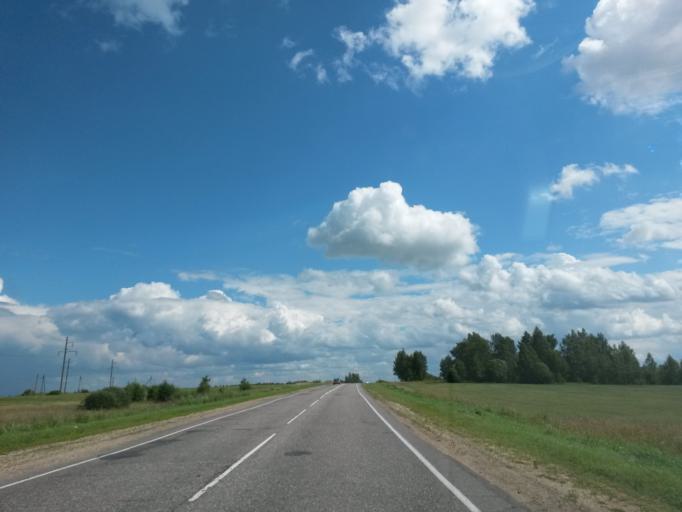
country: RU
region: Ivanovo
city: Pistsovo
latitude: 57.1867
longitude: 40.4537
